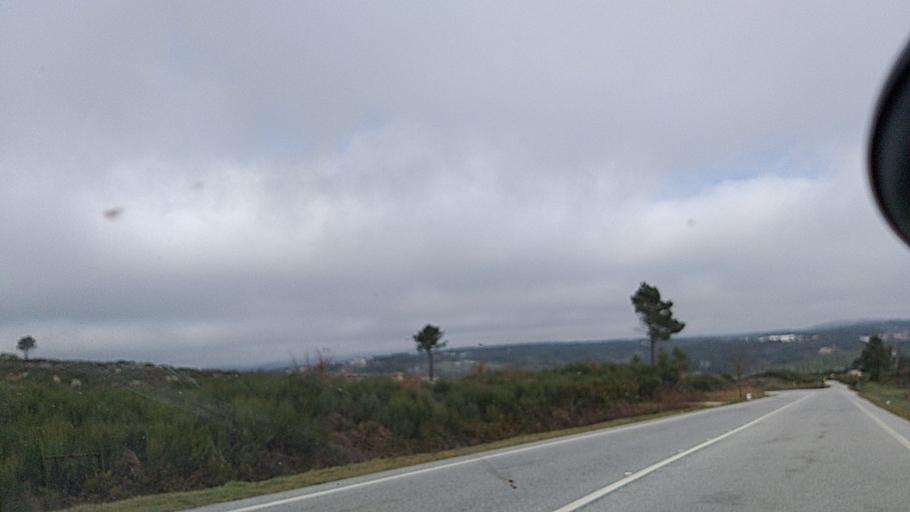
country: PT
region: Guarda
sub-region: Aguiar da Beira
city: Aguiar da Beira
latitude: 40.7692
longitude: -7.5032
